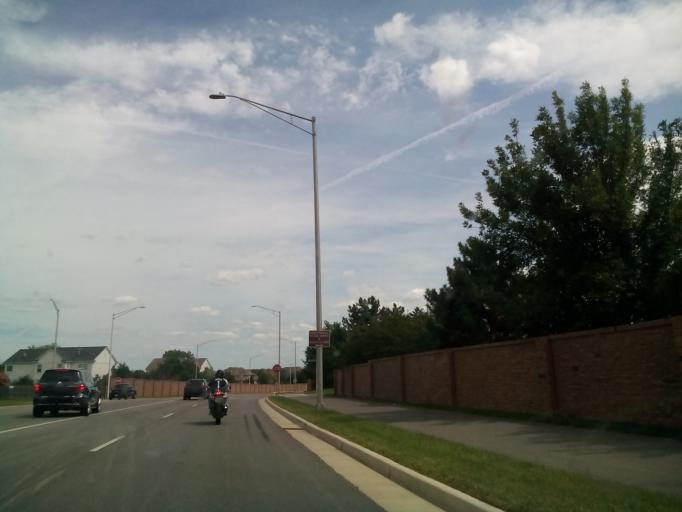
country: US
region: Illinois
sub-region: DuPage County
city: Naperville
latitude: 41.7100
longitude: -88.1608
